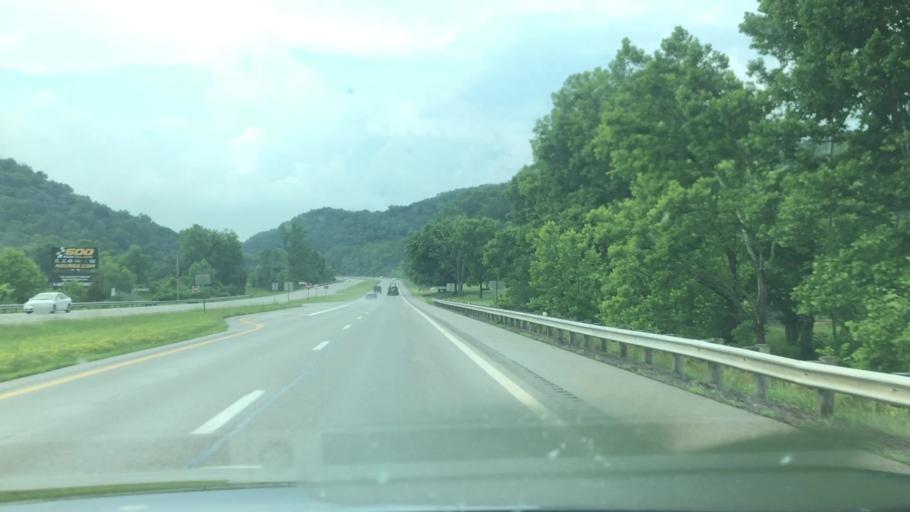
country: US
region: Ohio
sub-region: Jackson County
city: Jackson
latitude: 39.1458
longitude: -82.7267
